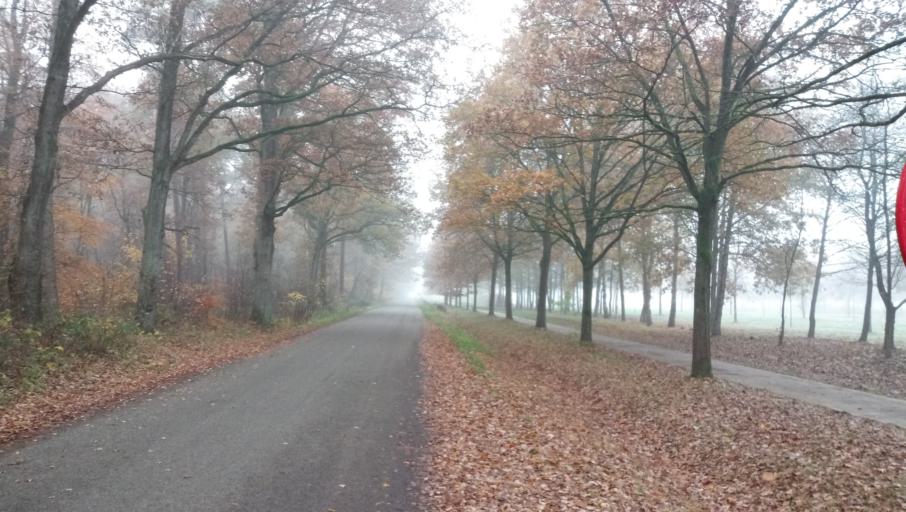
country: NL
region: Gelderland
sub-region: Gemeente Voorst
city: Twello
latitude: 52.1958
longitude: 6.1040
